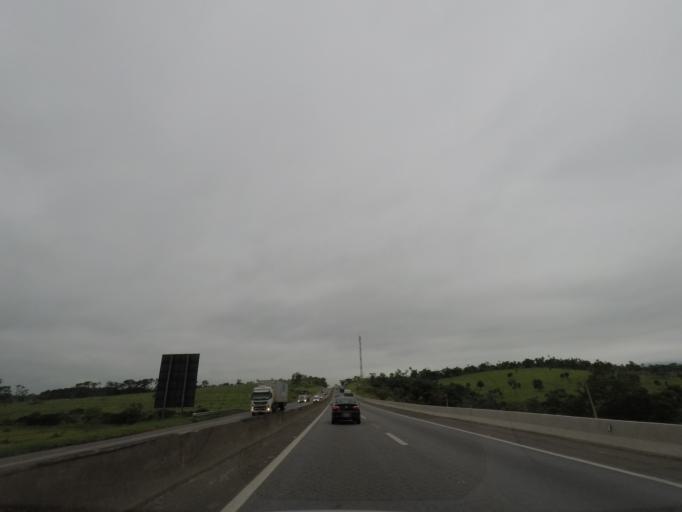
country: BR
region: Sao Paulo
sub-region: Pindamonhangaba
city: Pindamonhangaba
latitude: -22.9750
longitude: -45.4500
